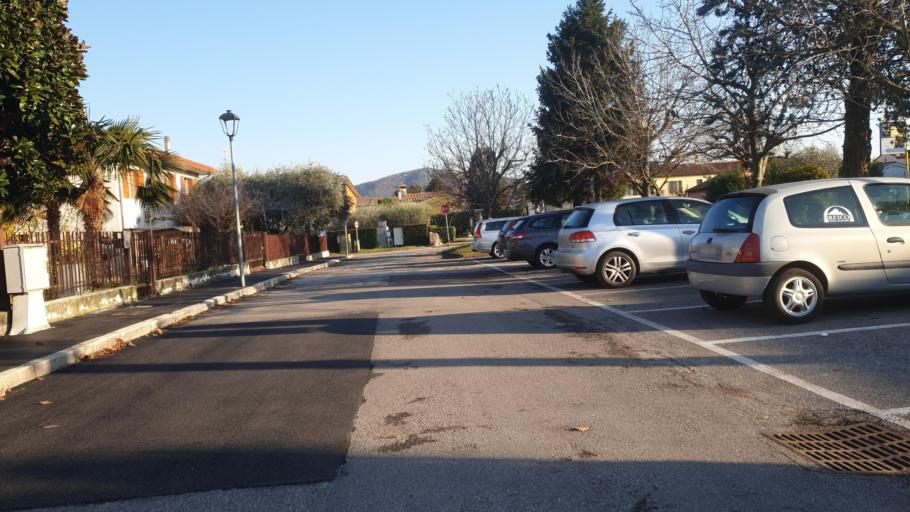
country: IT
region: Veneto
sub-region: Provincia di Padova
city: Galzignano
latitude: 45.3058
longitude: 11.7400
